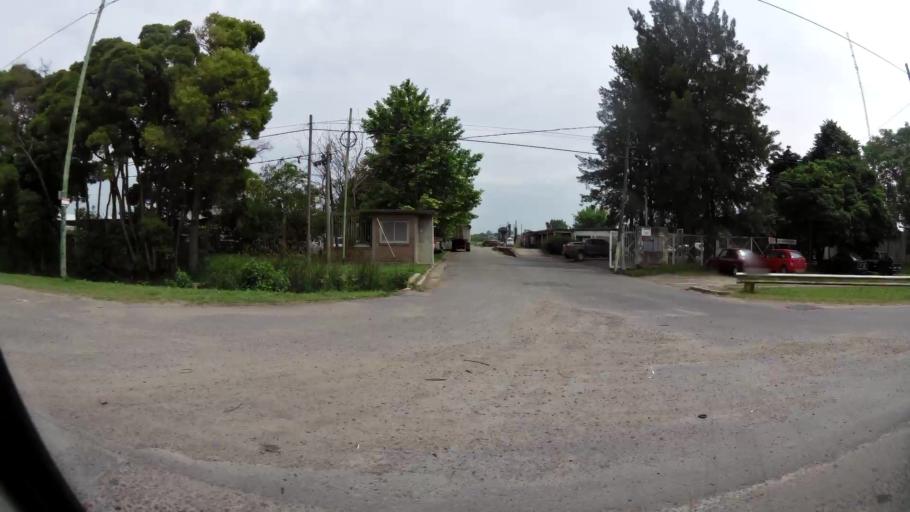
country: AR
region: Buenos Aires
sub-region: Partido de La Plata
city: La Plata
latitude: -34.9100
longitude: -58.0043
